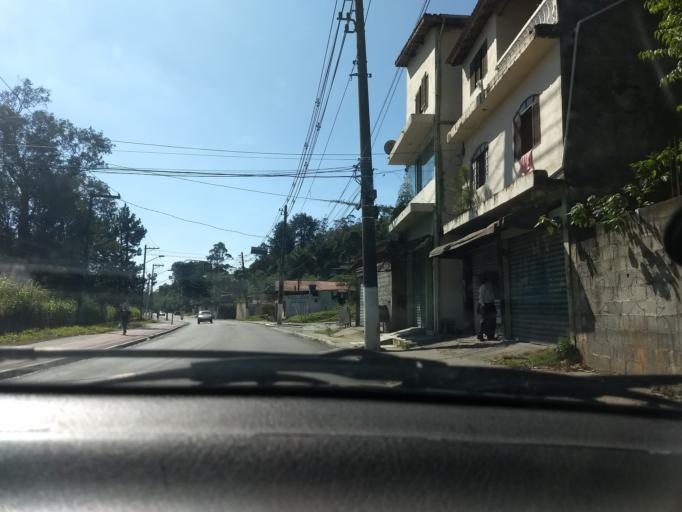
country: BR
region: Sao Paulo
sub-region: Embu-Guacu
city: Embu Guacu
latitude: -23.8353
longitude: -46.7305
